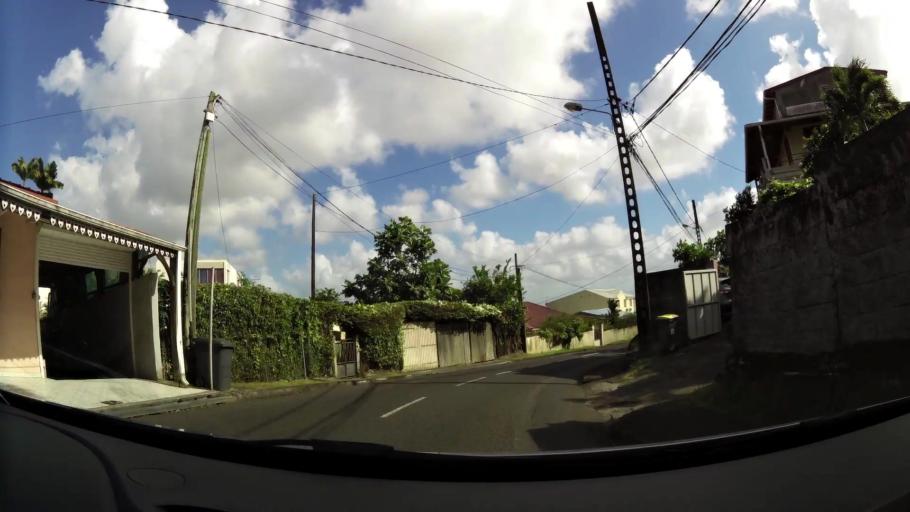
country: MQ
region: Martinique
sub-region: Martinique
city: Fort-de-France
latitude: 14.6235
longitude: -61.0610
